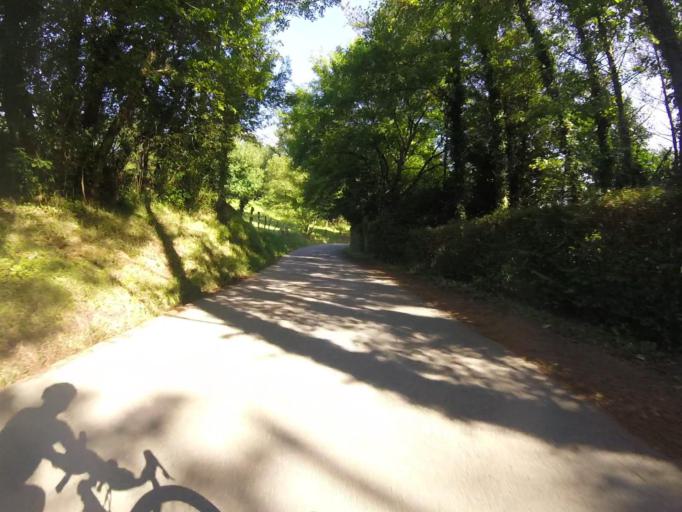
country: ES
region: Basque Country
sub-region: Provincia de Guipuzcoa
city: Astigarraga
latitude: 43.2674
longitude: -1.9302
